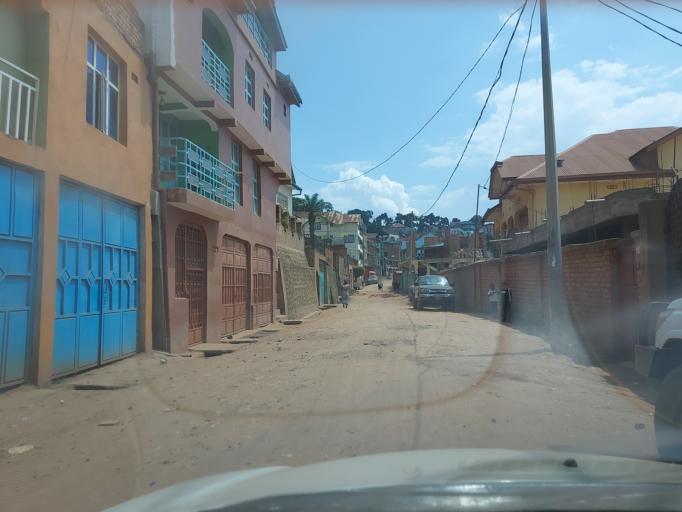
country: CD
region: South Kivu
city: Bukavu
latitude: -2.5006
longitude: 28.8626
